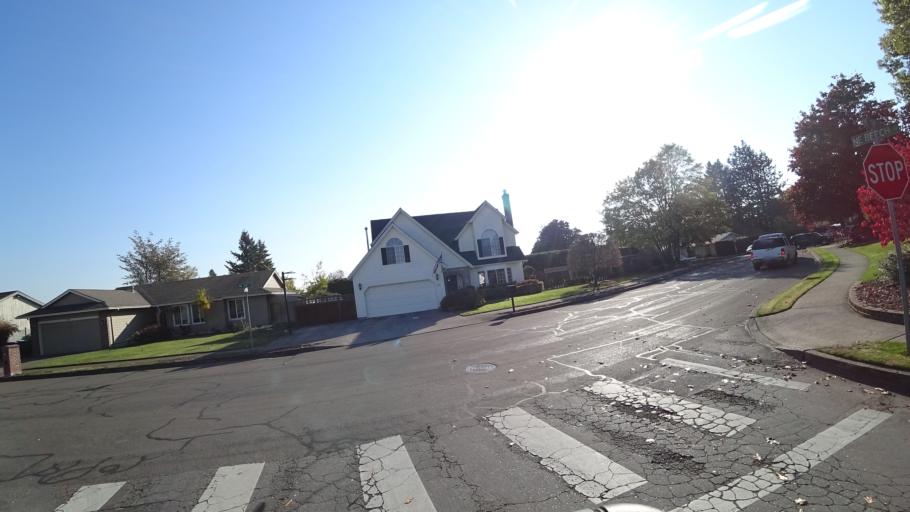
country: US
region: Oregon
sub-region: Multnomah County
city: Gresham
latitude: 45.5137
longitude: -122.4265
